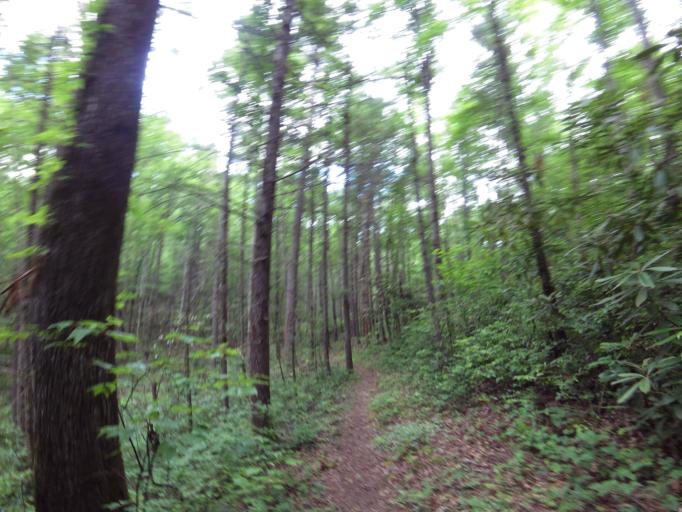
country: US
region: Tennessee
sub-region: Blount County
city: Wildwood
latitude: 35.6704
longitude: -83.8306
